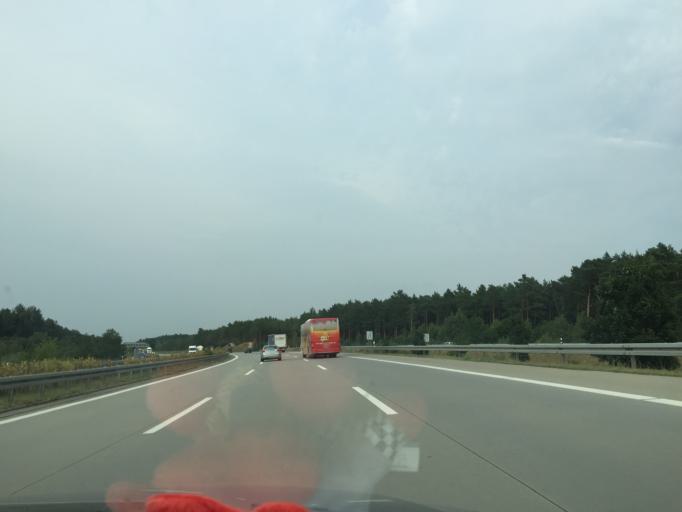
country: DE
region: Brandenburg
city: Erkner
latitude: 52.3274
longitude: 13.7493
